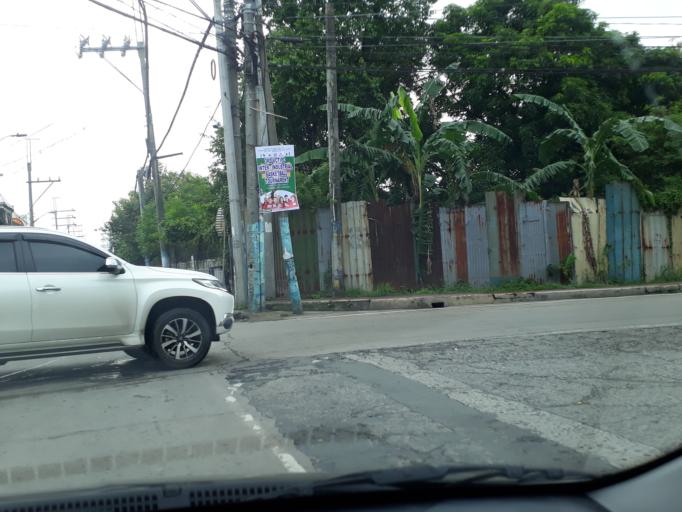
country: PH
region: Calabarzon
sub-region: Province of Rizal
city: Valenzuela
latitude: 14.7122
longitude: 120.9672
